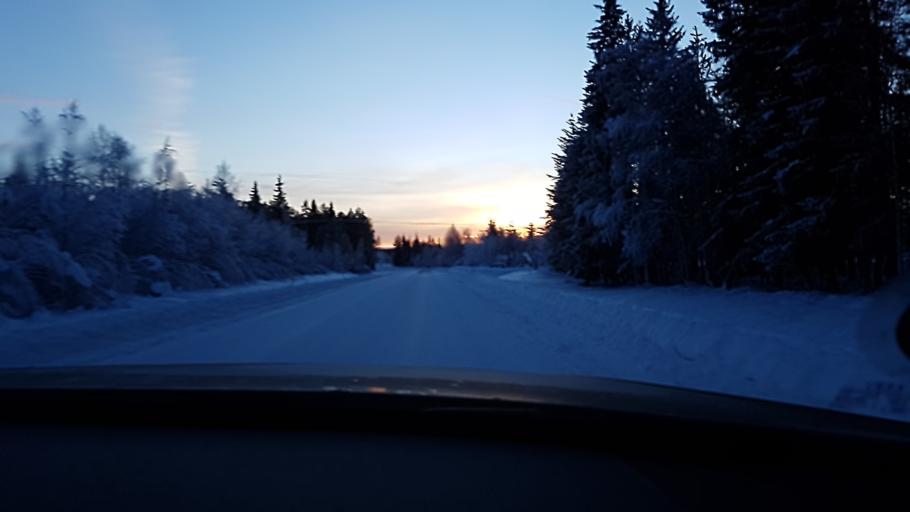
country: SE
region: Vaesterbotten
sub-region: Storumans Kommun
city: Storuman
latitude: 65.1549
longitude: 17.2610
